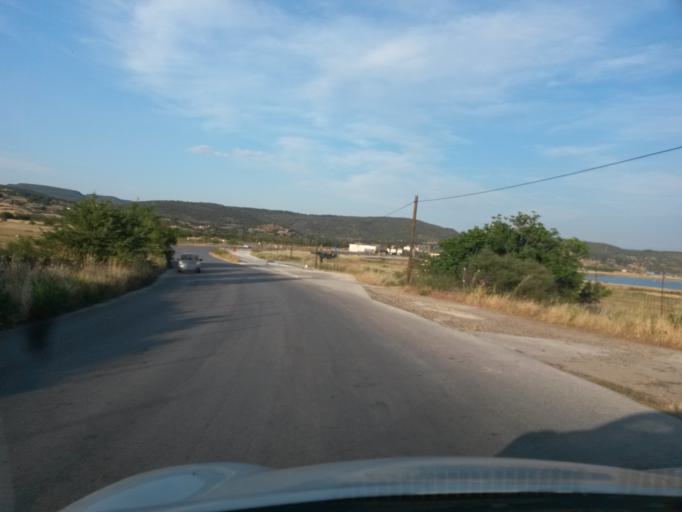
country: GR
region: North Aegean
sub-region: Nomos Lesvou
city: Kalloni
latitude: 39.2251
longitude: 26.2396
